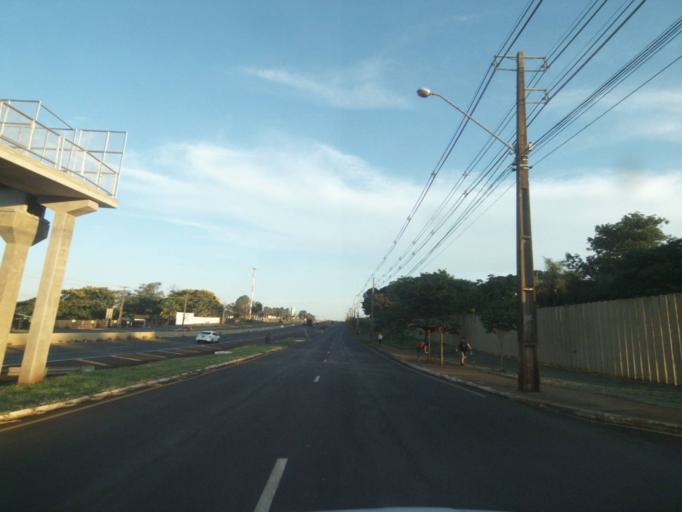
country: BR
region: Parana
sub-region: Londrina
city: Londrina
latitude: -23.3542
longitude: -51.1616
